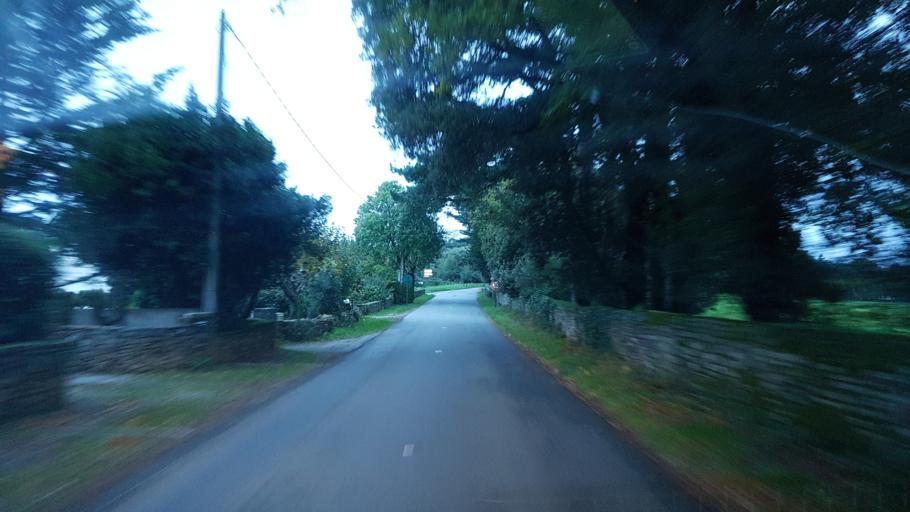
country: FR
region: Brittany
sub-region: Departement du Morbihan
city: Sarzeau
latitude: 47.5366
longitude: -2.7783
